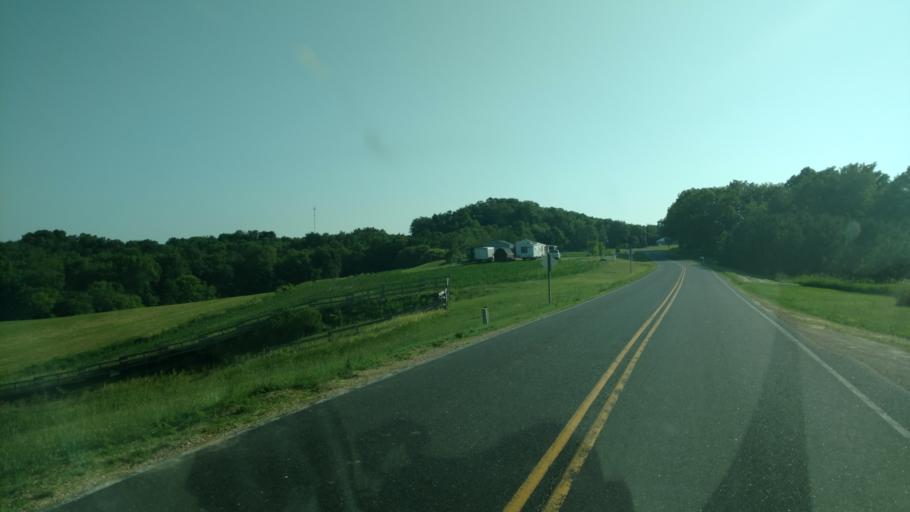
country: US
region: Wisconsin
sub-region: Vernon County
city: Hillsboro
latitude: 43.6827
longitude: -90.3448
